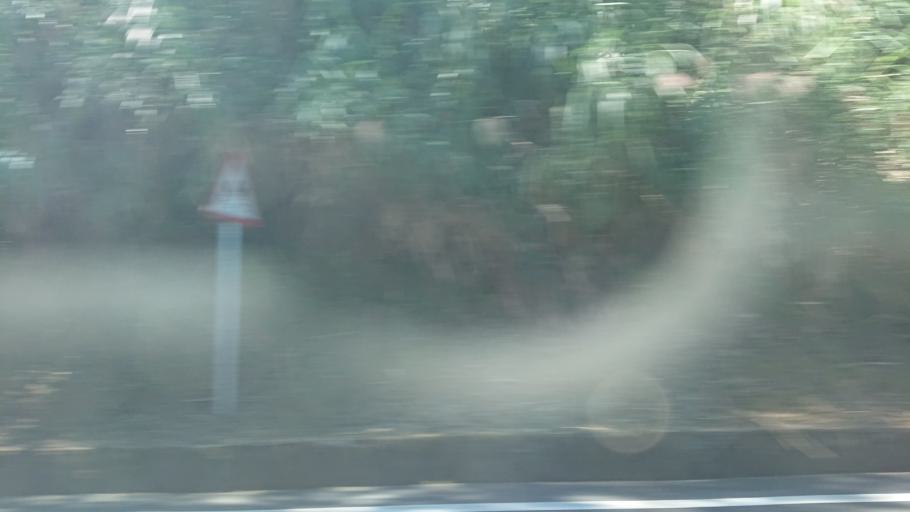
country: TW
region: Taiwan
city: Lugu
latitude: 23.4782
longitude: 120.8344
